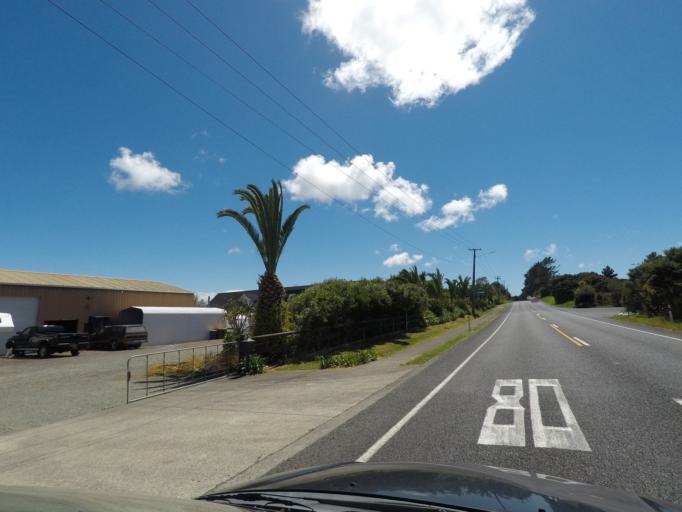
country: NZ
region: Auckland
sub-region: Auckland
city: Rothesay Bay
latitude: -36.7489
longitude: 174.6704
